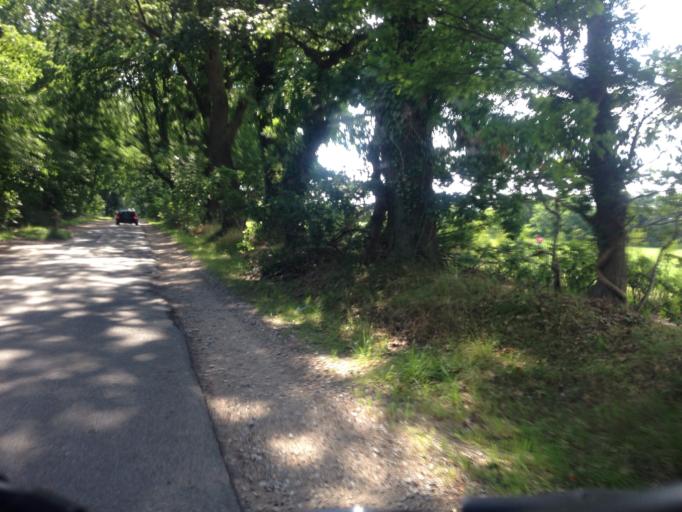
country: DE
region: Lower Saxony
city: Adendorf
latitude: 53.2938
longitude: 10.4493
